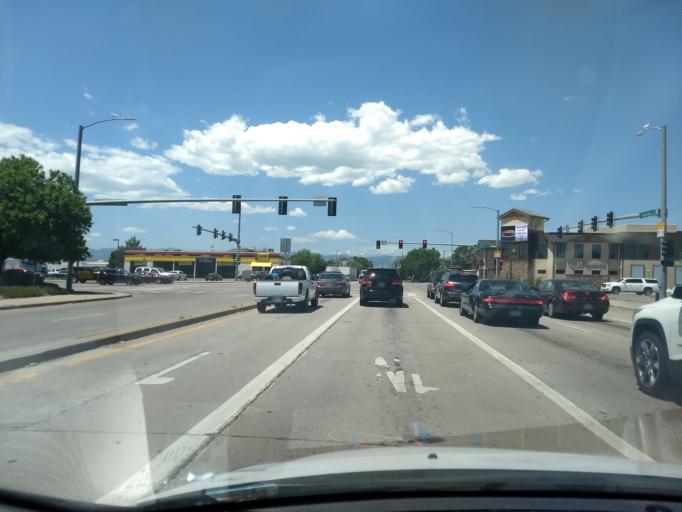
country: US
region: Colorado
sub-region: Arapahoe County
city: Englewood
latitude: 39.6241
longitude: -104.9873
